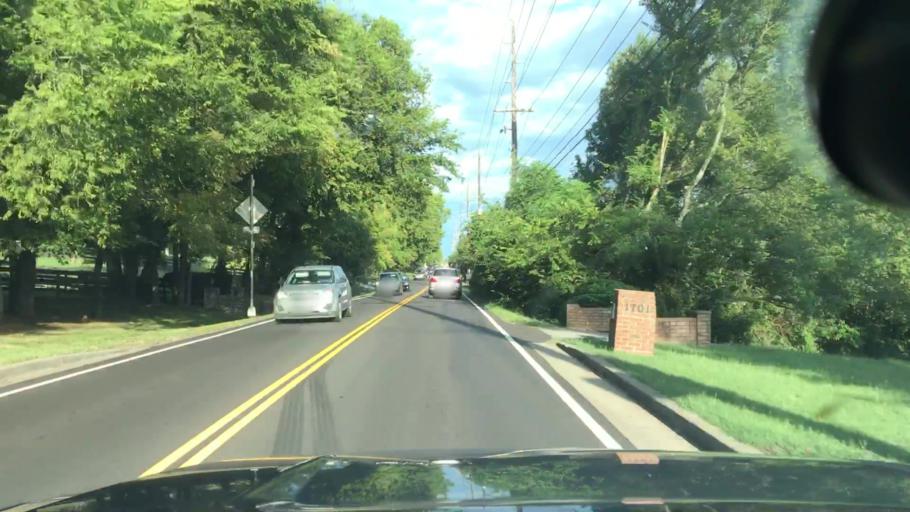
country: US
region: Tennessee
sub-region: Davidson County
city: Forest Hills
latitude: 36.0428
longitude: -86.8407
